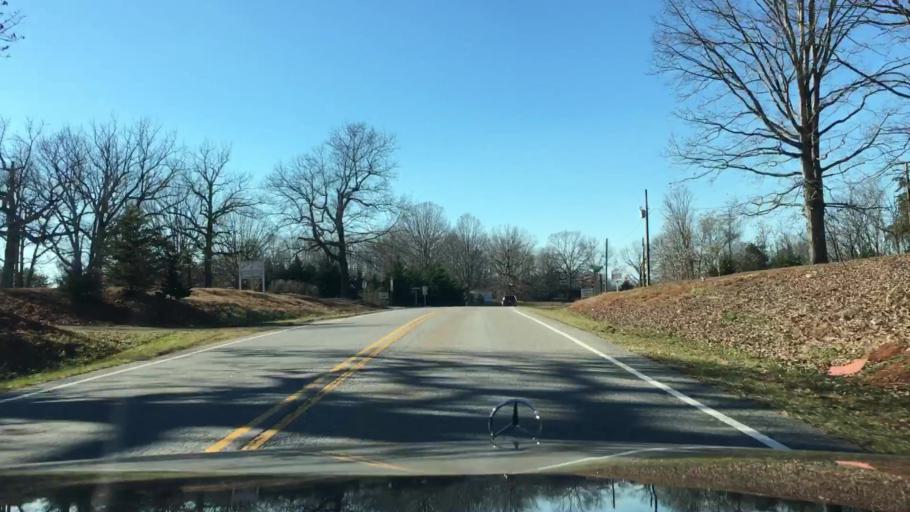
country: US
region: Virginia
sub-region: City of Bedford
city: Bedford
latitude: 37.2227
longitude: -79.5125
